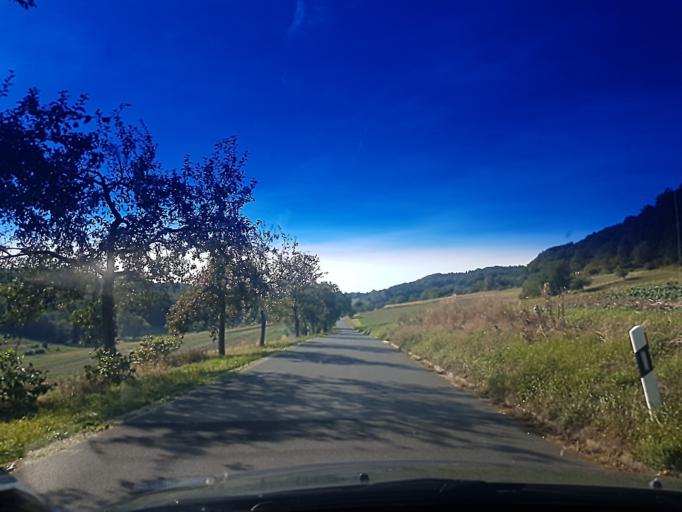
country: DE
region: Bavaria
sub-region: Upper Franconia
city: Schesslitz
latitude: 50.0095
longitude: 11.0534
